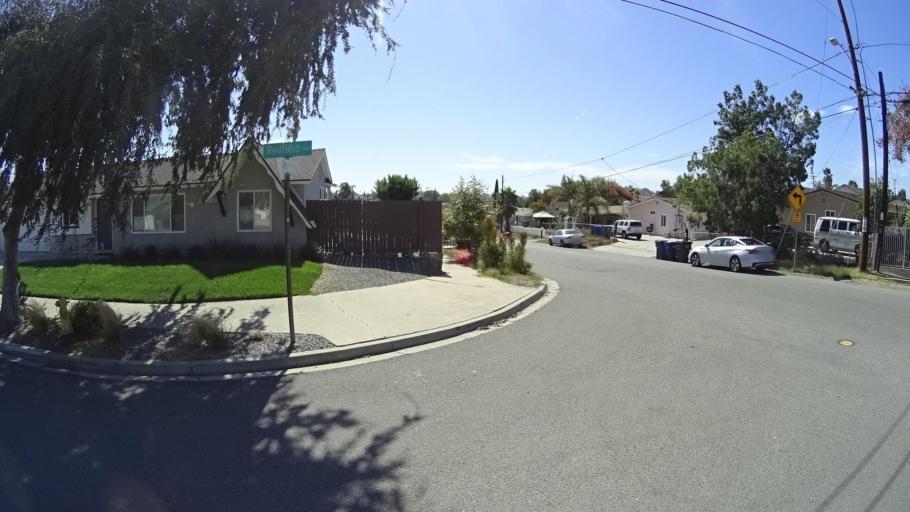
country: US
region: California
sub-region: San Diego County
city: La Presa
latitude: 32.7109
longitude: -117.0059
